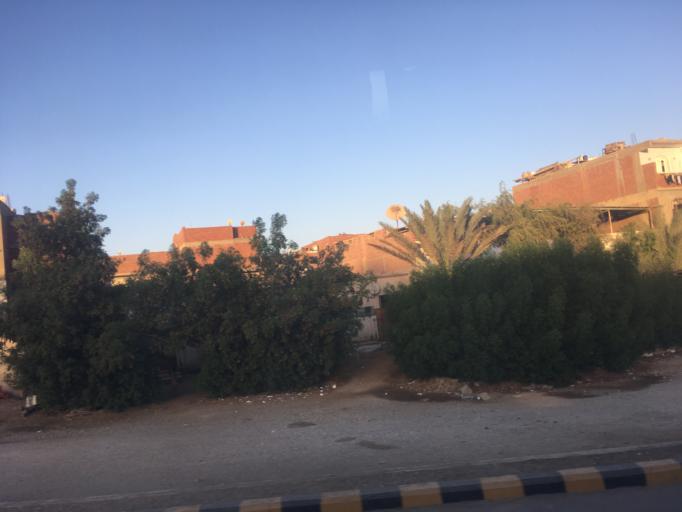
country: EG
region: Red Sea
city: Al Qusayr
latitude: 26.1169
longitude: 34.2749
